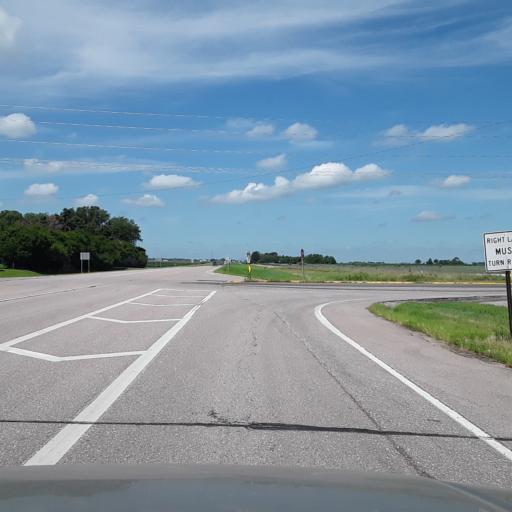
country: US
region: Nebraska
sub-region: York County
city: York
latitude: 40.9017
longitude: -97.4056
